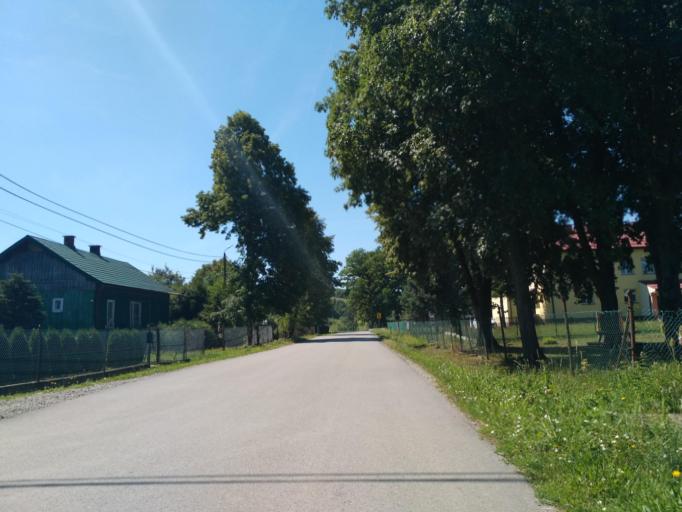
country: PL
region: Subcarpathian Voivodeship
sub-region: Powiat sanocki
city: Nowosielce-Gniewosz
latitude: 49.5411
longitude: 22.0578
